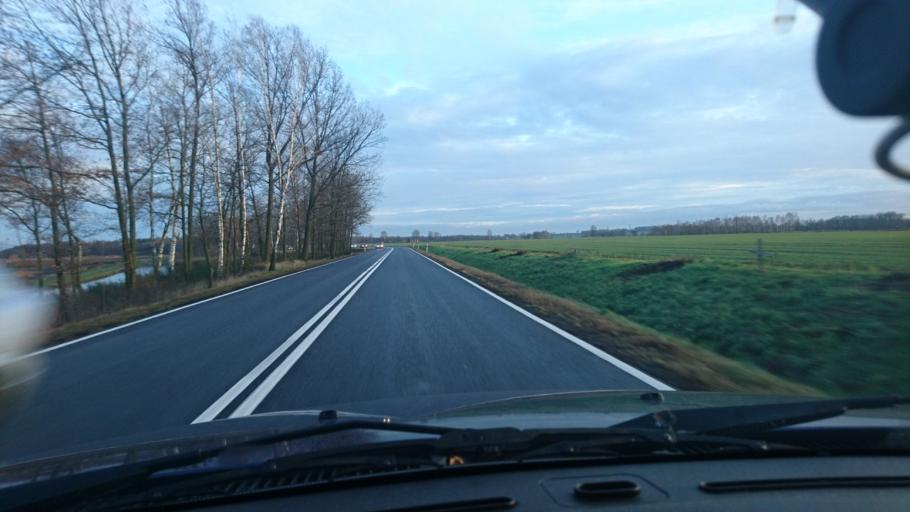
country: PL
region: Lodz Voivodeship
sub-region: Powiat wieruszowski
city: Boleslawiec
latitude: 51.1578
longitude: 18.1677
